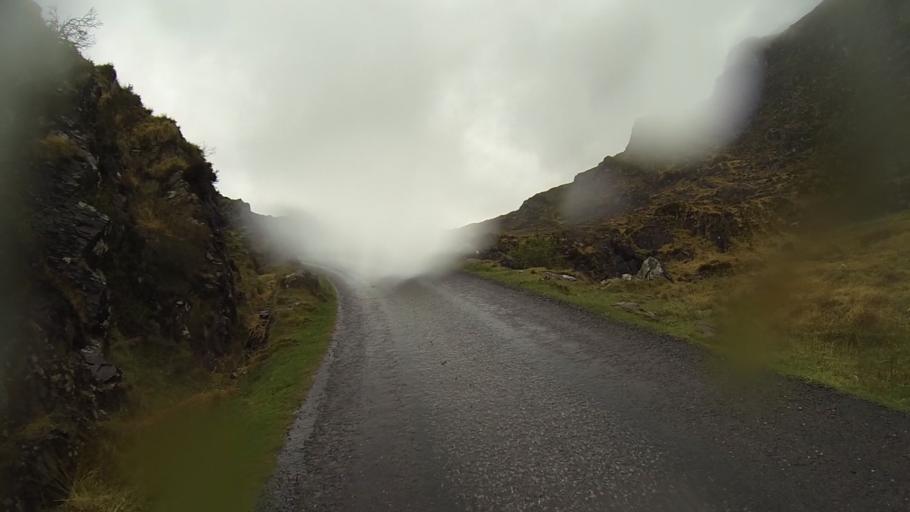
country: IE
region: Munster
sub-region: Ciarrai
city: Kenmare
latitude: 51.9975
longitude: -9.6438
